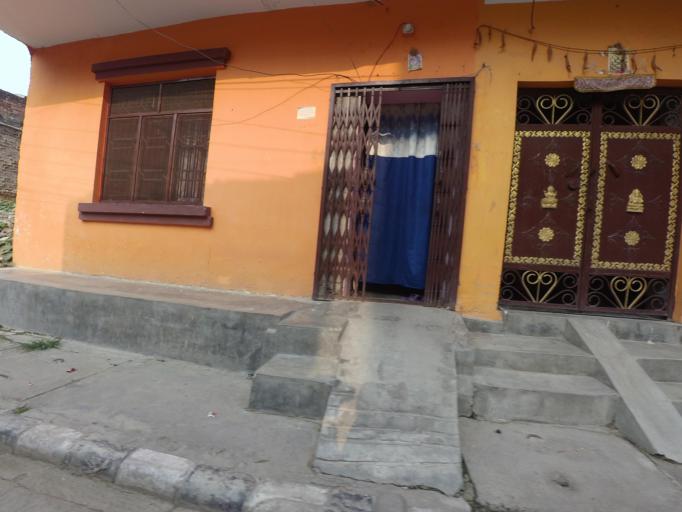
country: NP
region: Western Region
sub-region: Lumbini Zone
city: Bhairahawa
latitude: 27.5101
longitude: 83.4523
